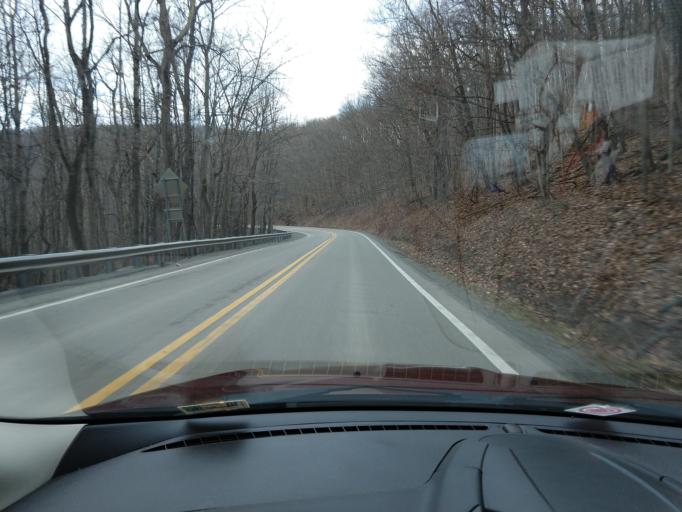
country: US
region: West Virginia
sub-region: Randolph County
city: Elkins
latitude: 38.6611
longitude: -79.9230
